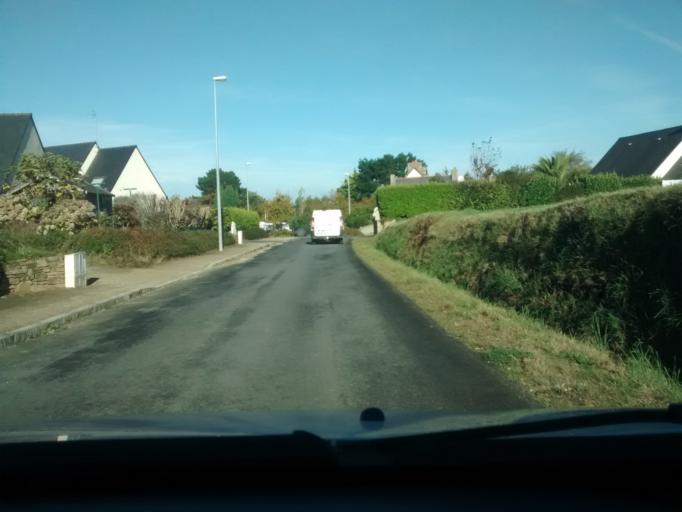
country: FR
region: Brittany
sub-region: Departement des Cotes-d'Armor
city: Louannec
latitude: 48.7898
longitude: -3.4120
